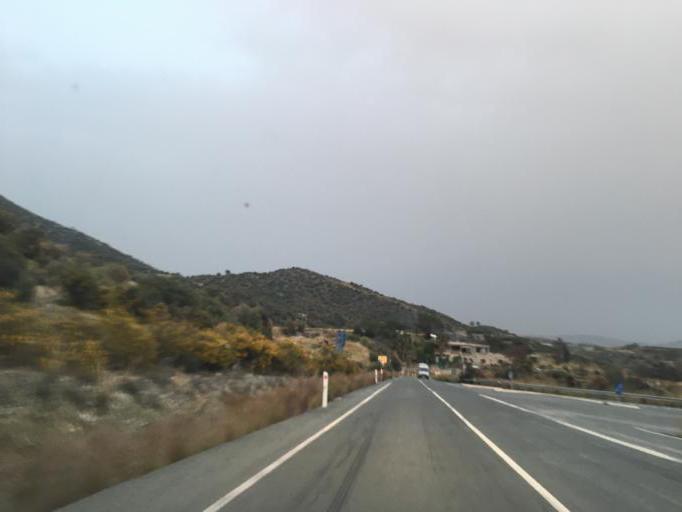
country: CY
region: Limassol
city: Parekklisha
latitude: 34.7869
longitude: 33.1630
